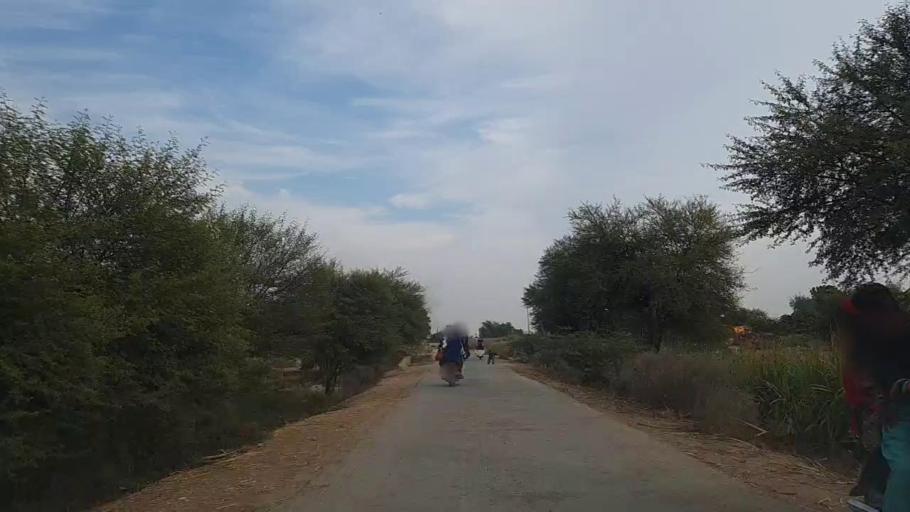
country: PK
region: Sindh
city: Daur
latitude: 26.5268
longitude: 68.4113
